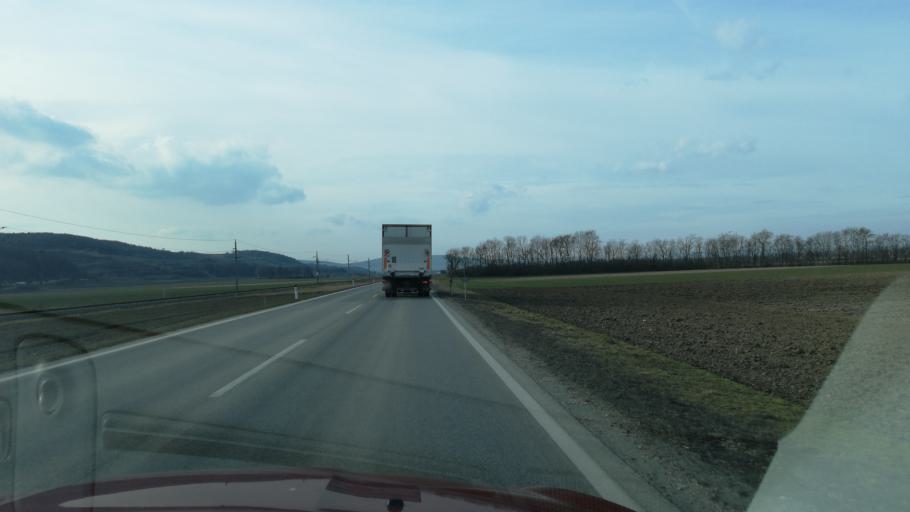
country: AT
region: Lower Austria
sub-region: Politischer Bezirk Tulln
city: Grafenworth
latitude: 48.3386
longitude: 15.7968
